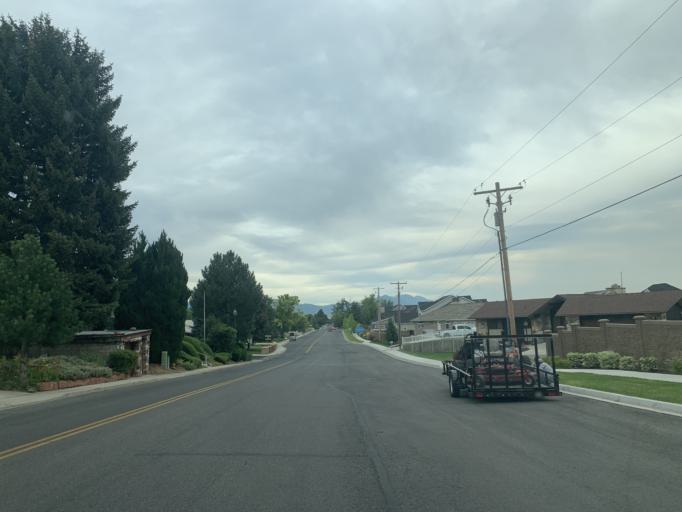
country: US
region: Utah
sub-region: Utah County
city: Orem
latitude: 40.2597
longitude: -111.6949
